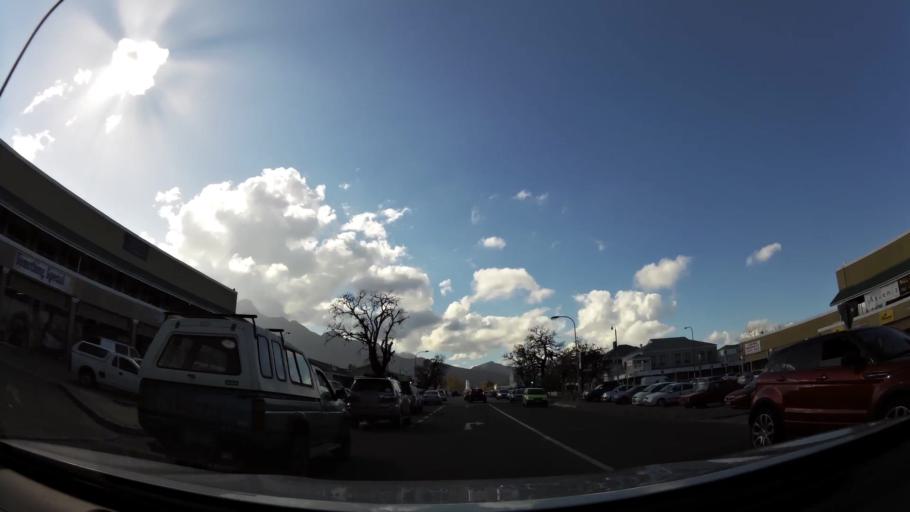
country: ZA
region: Western Cape
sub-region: Eden District Municipality
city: George
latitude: -33.9624
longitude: 22.4582
